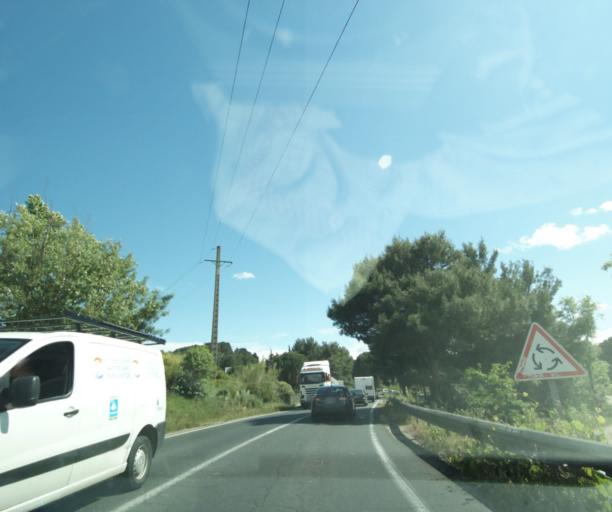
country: FR
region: Languedoc-Roussillon
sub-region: Departement de l'Herault
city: Laverune
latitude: 43.5940
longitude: 3.8205
